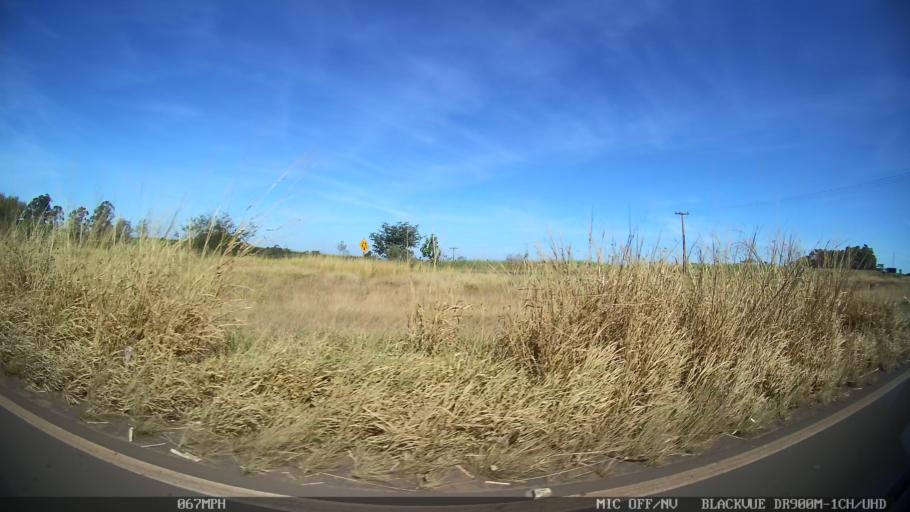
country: BR
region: Sao Paulo
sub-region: Franca
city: Franca
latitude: -20.5559
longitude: -47.5696
